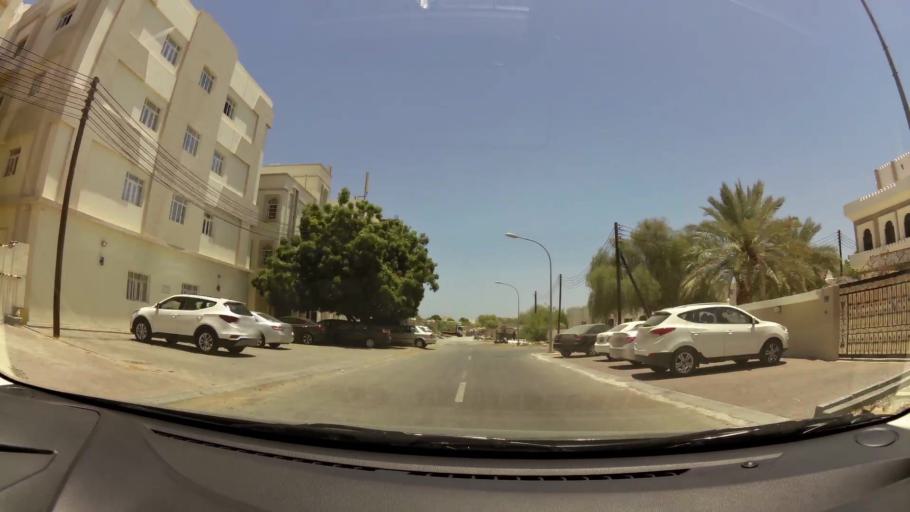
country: OM
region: Muhafazat Masqat
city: As Sib al Jadidah
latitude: 23.6375
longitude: 58.2341
